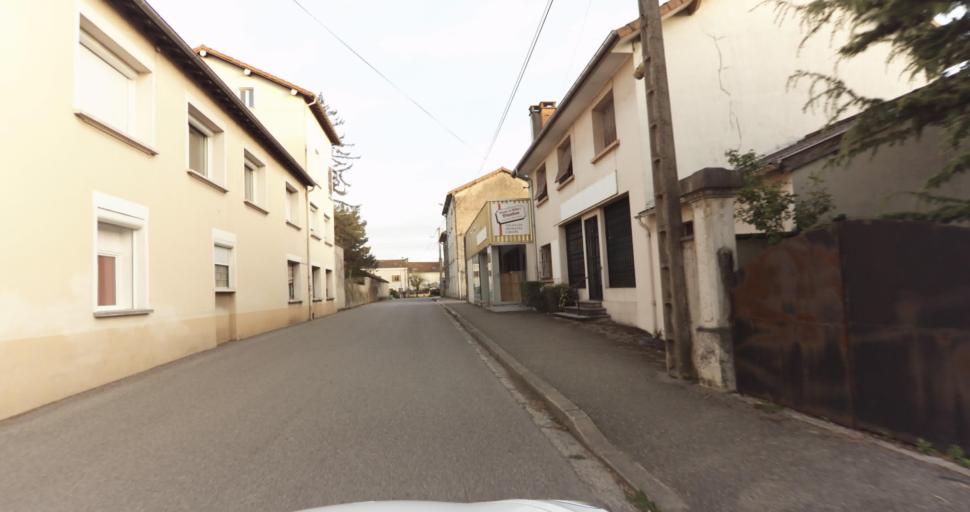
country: FR
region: Rhone-Alpes
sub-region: Departement de l'Ain
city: Amberieu-en-Bugey
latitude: 45.9578
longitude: 5.3478
